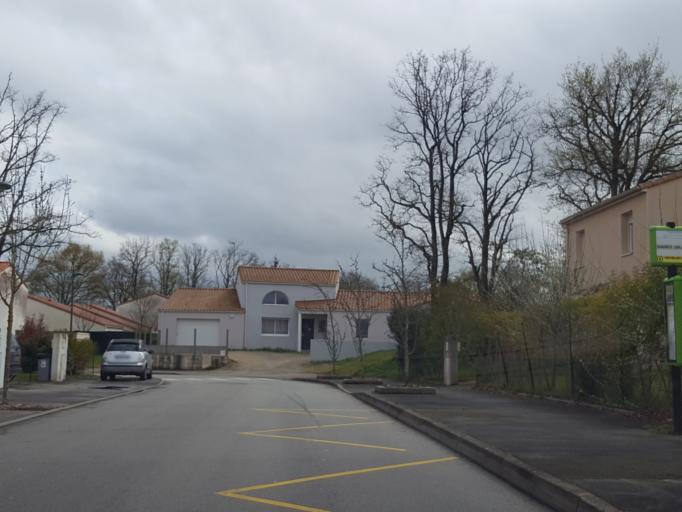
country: FR
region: Pays de la Loire
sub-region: Departement de la Vendee
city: La Roche-sur-Yon
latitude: 46.6678
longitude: -1.3972
